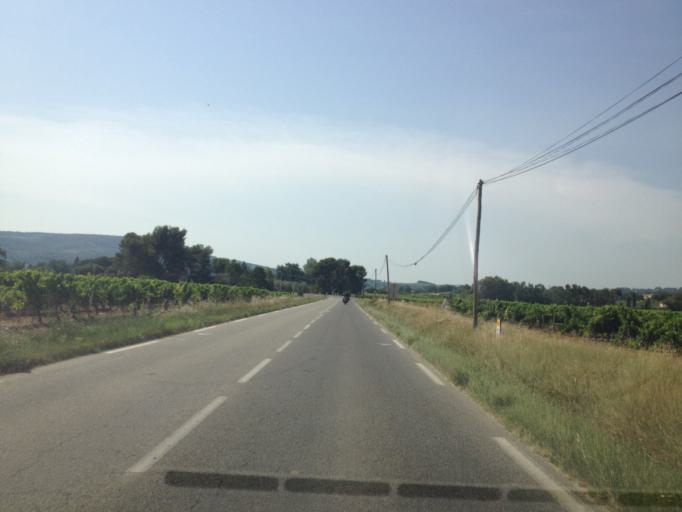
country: FR
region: Provence-Alpes-Cote d'Azur
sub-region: Departement du Vaucluse
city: Vaison-la-Romaine
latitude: 44.2482
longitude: 5.0453
